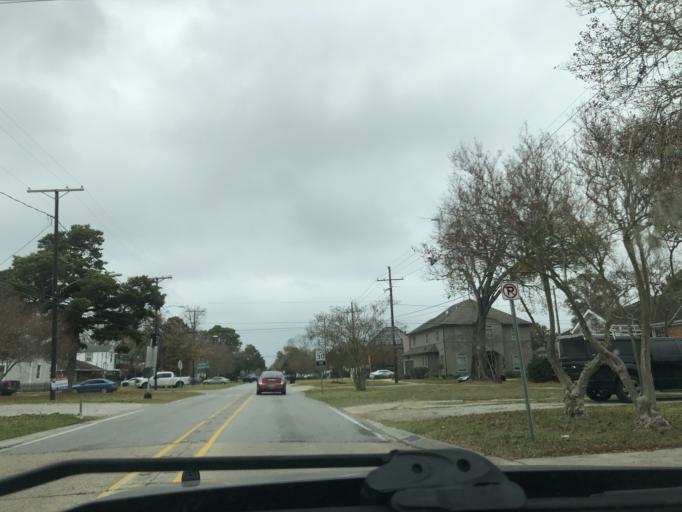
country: US
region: Louisiana
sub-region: Jefferson Parish
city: Metairie Terrace
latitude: 29.9768
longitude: -90.1605
